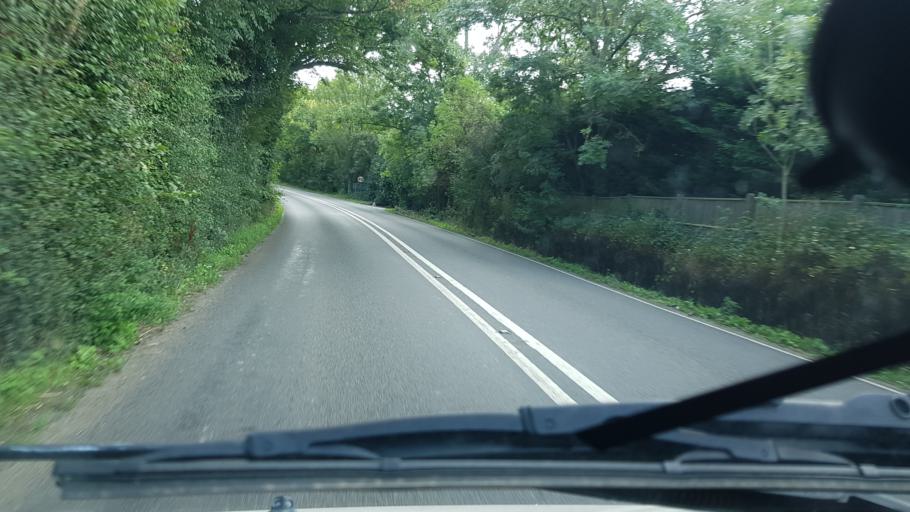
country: GB
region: England
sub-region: West Sussex
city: Rudgwick
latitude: 51.0854
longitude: -0.4510
